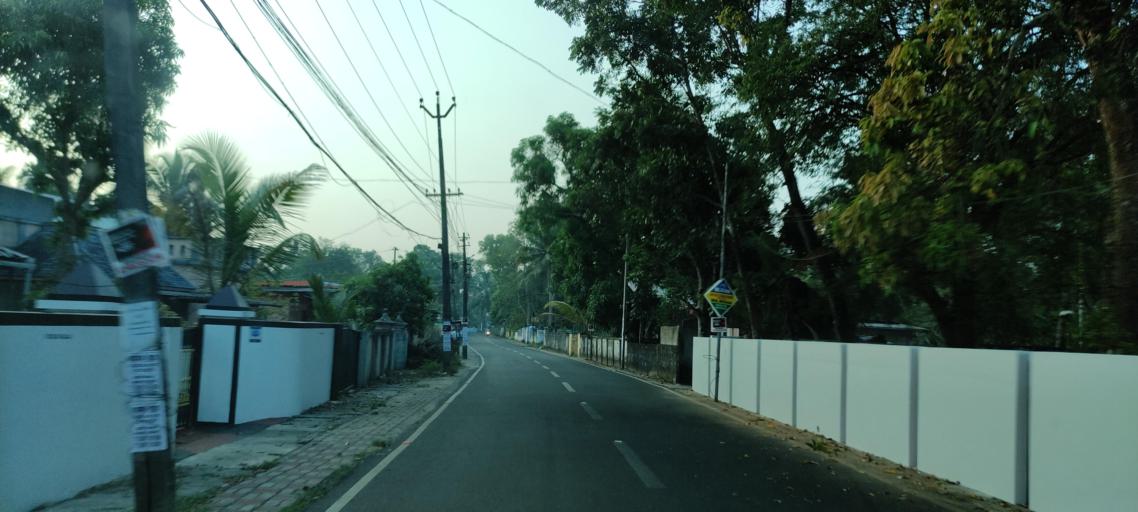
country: IN
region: Kerala
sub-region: Alappuzha
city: Alleppey
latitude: 9.4502
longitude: 76.3453
